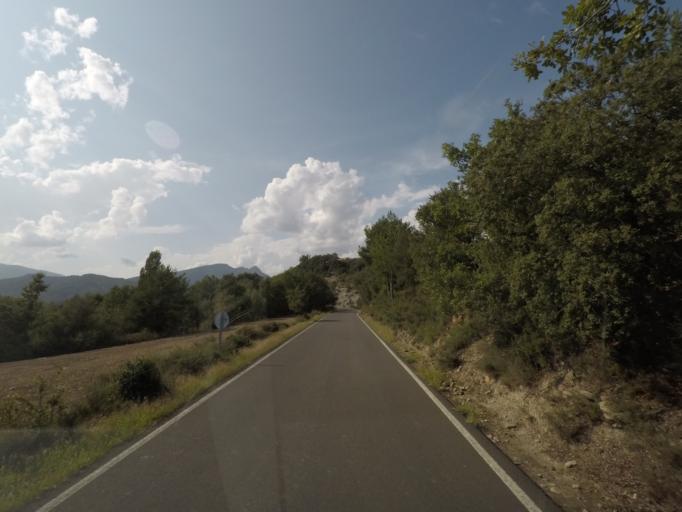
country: ES
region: Aragon
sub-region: Provincia de Huesca
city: Laspuna
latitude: 42.5017
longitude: 0.1403
